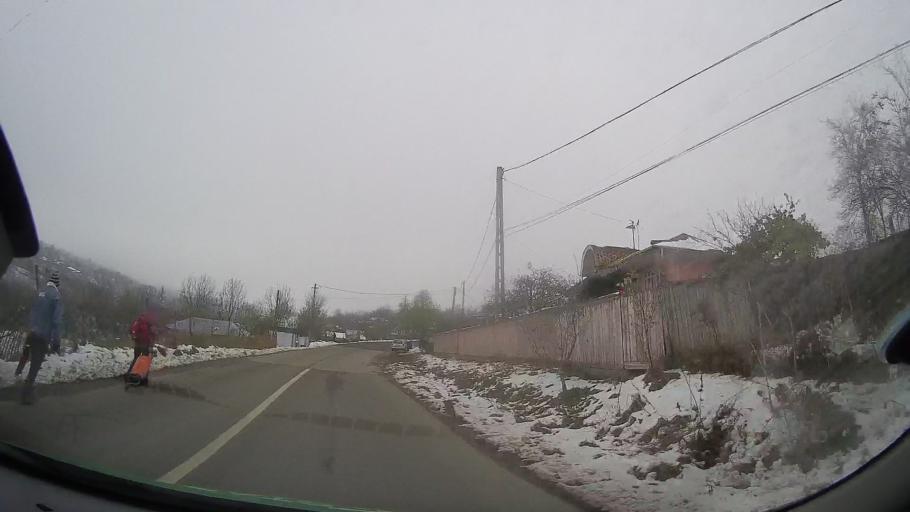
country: RO
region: Vrancea
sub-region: Comuna Boghesti
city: Boghesti
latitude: 46.2075
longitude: 27.4412
